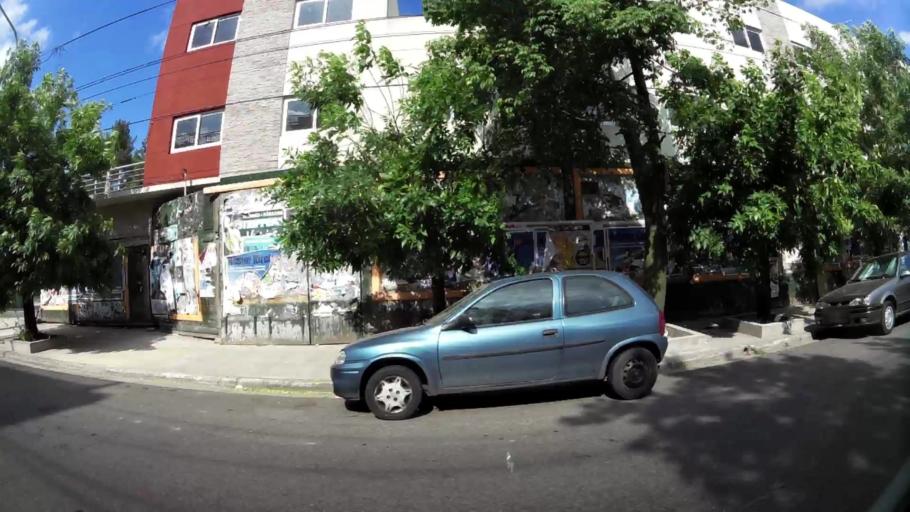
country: AR
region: Buenos Aires
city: San Justo
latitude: -34.6620
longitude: -58.5617
